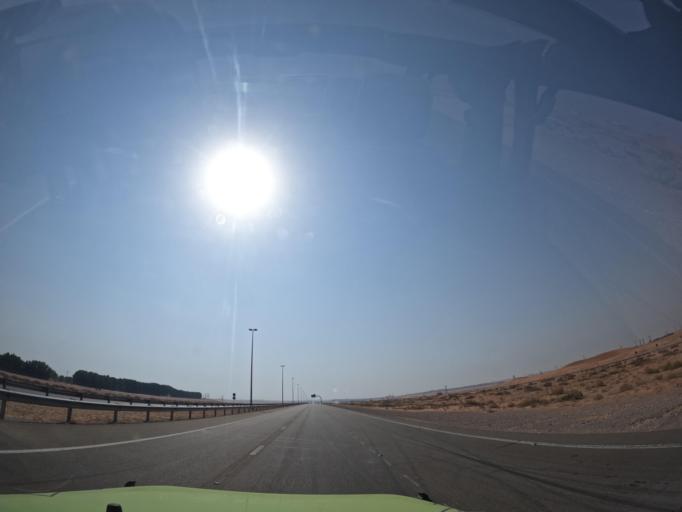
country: OM
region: Al Buraimi
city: Al Buraymi
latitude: 24.4158
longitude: 55.6954
